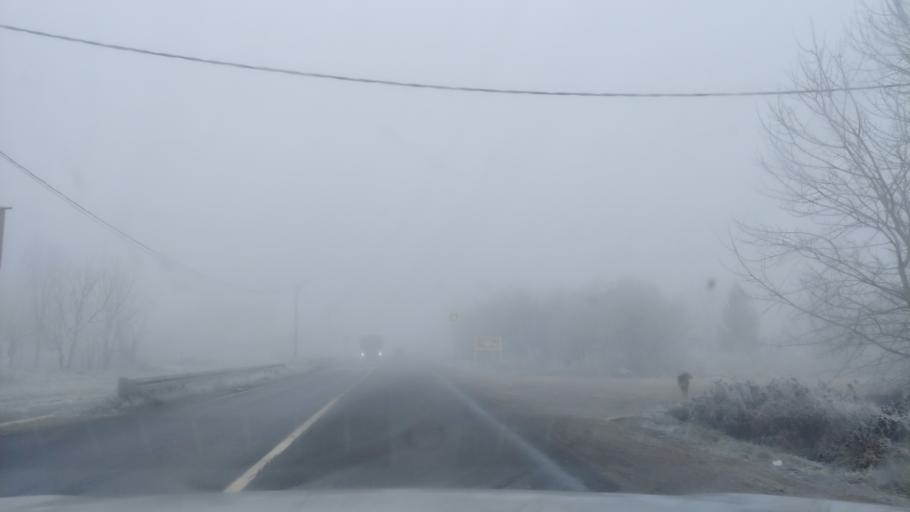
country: RS
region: Central Serbia
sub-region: Belgrade
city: Zemun
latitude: 44.8940
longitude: 20.4565
